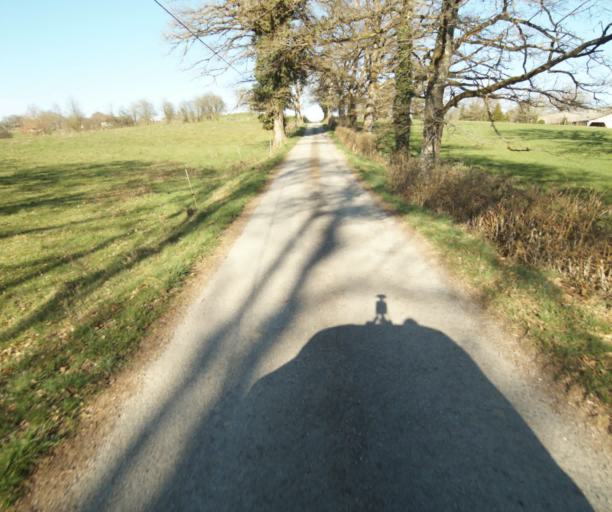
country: FR
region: Limousin
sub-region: Departement de la Correze
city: Chamboulive
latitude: 45.4939
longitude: 1.7267
